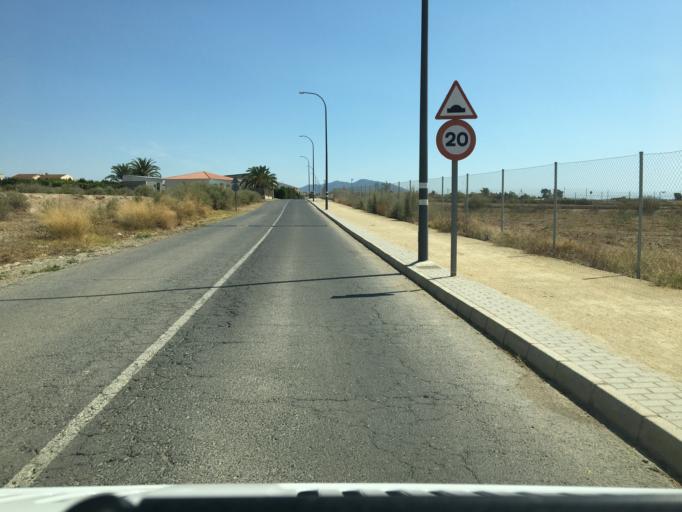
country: ES
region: Andalusia
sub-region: Provincia de Almeria
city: Huercal-Overa
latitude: 37.4050
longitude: -1.9337
